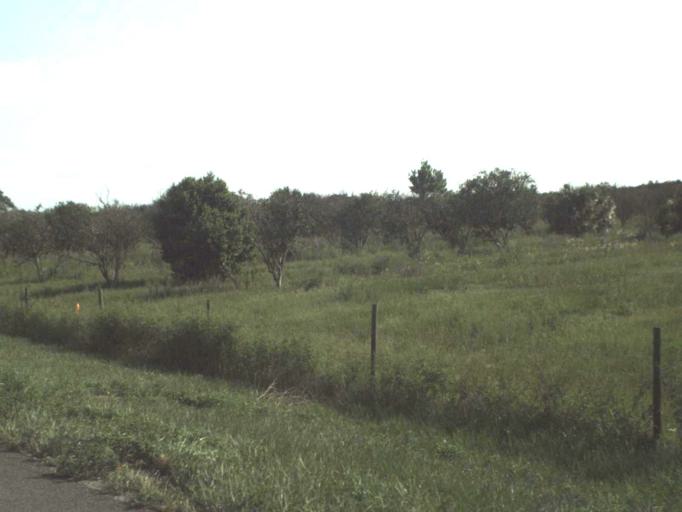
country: US
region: Florida
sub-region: Lake County
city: Groveland
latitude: 28.5461
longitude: -81.8516
